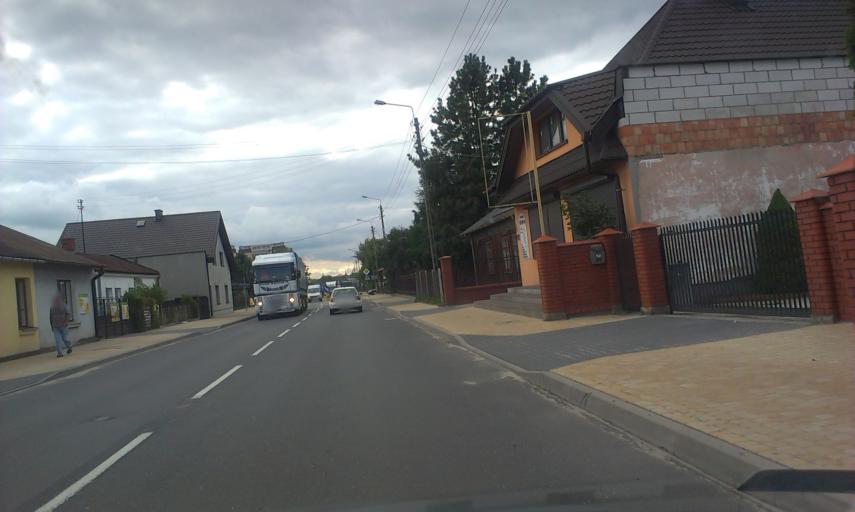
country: PL
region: Masovian Voivodeship
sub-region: Powiat zyrardowski
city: Mszczonow
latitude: 51.9740
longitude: 20.5260
